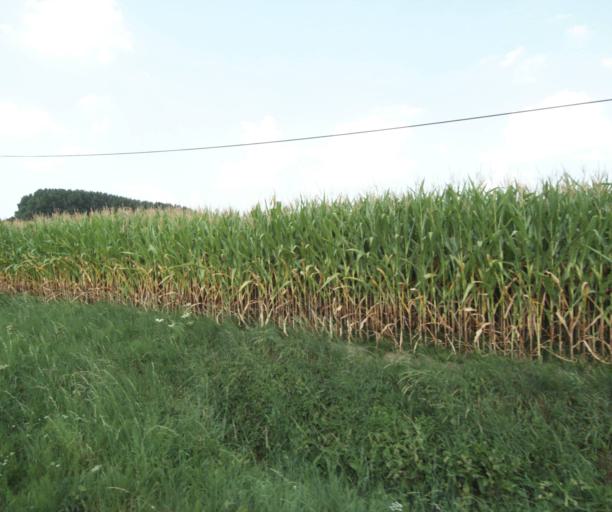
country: FR
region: Nord-Pas-de-Calais
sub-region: Departement du Nord
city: Comines
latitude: 50.7399
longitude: 3.0219
